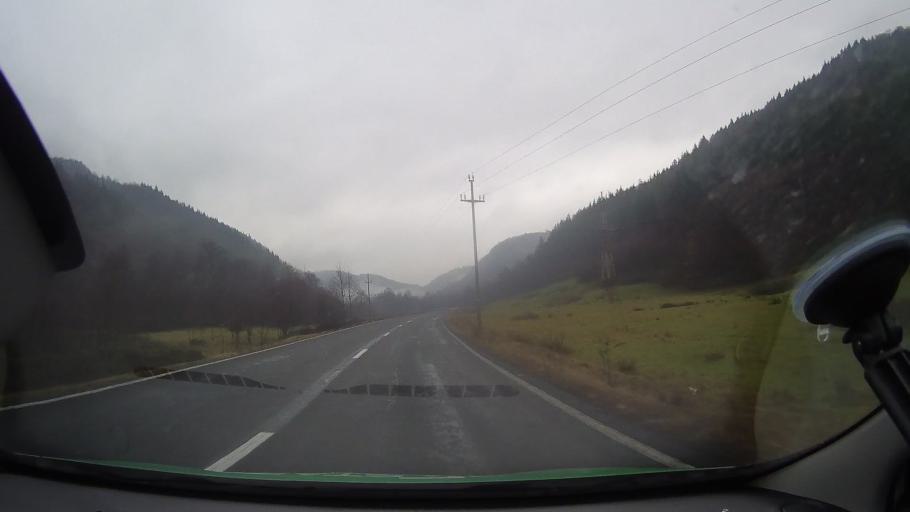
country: RO
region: Arad
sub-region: Comuna Plescuta
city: Plescuta
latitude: 46.3050
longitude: 22.4559
